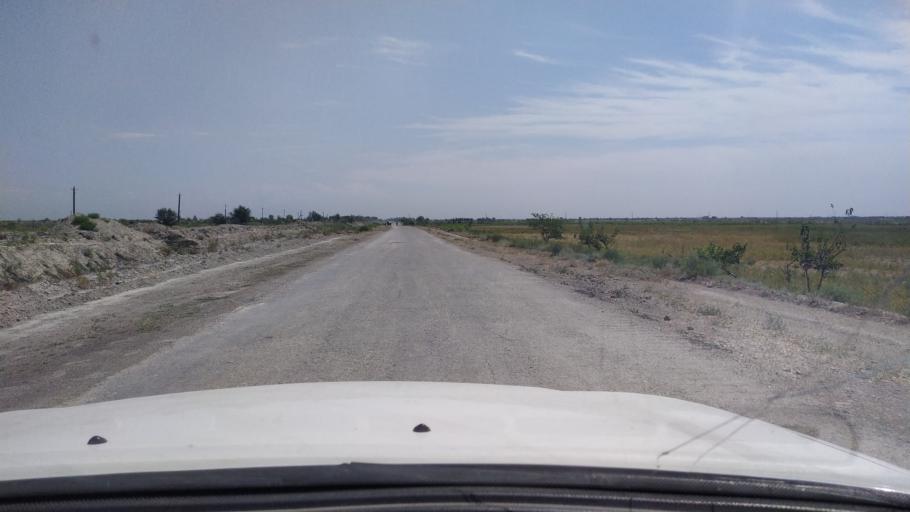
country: UZ
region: Namangan
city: Toshbuloq
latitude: 40.7908
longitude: 71.5686
